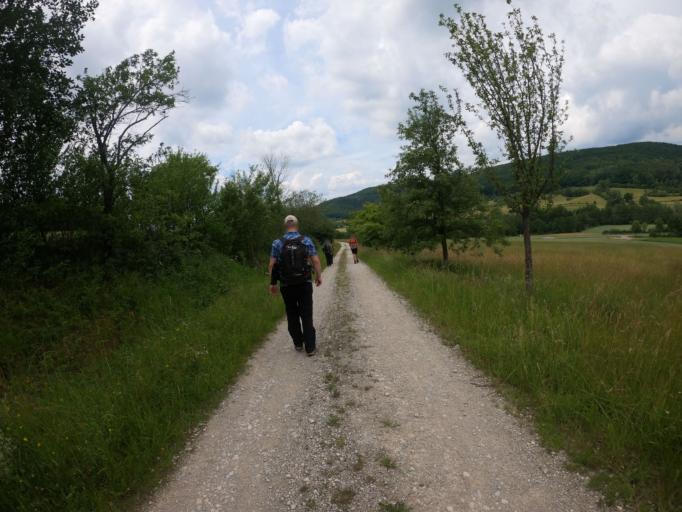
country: DE
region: Bavaria
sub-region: Upper Franconia
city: Litzendorf
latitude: 49.9155
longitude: 11.0600
